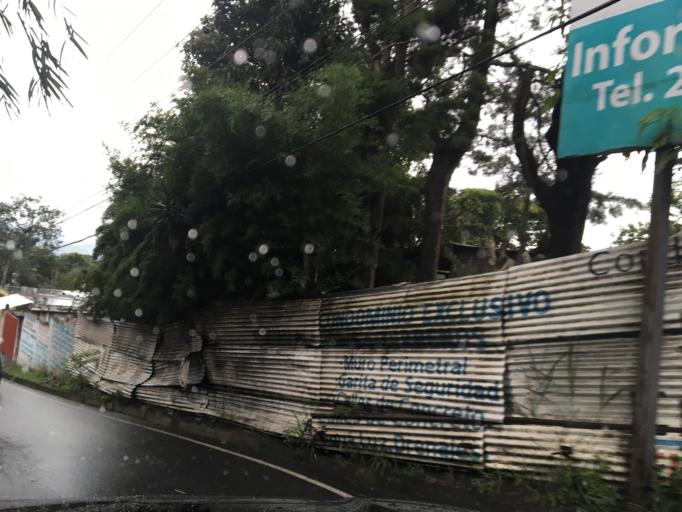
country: GT
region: Guatemala
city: Santa Catarina Pinula
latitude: 14.5454
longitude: -90.5148
